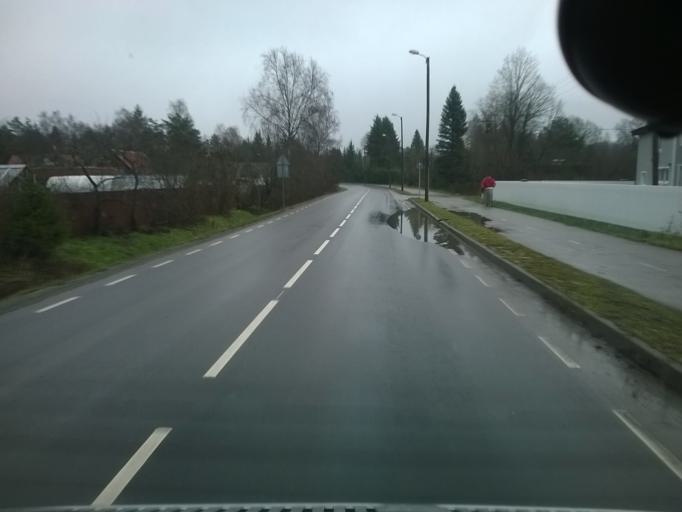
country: EE
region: Harju
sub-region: Saku vald
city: Saku
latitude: 59.2182
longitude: 24.6663
